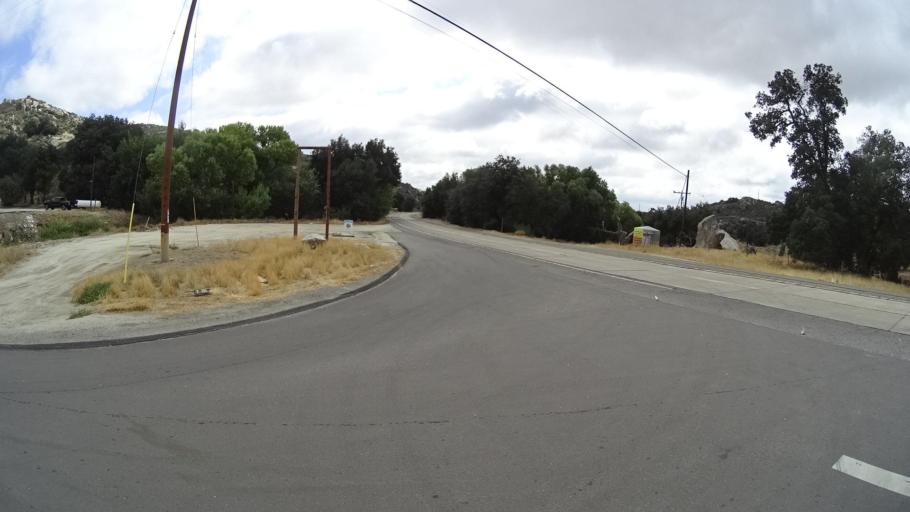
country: US
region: California
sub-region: San Diego County
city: Campo
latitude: 32.6872
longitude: -116.3362
